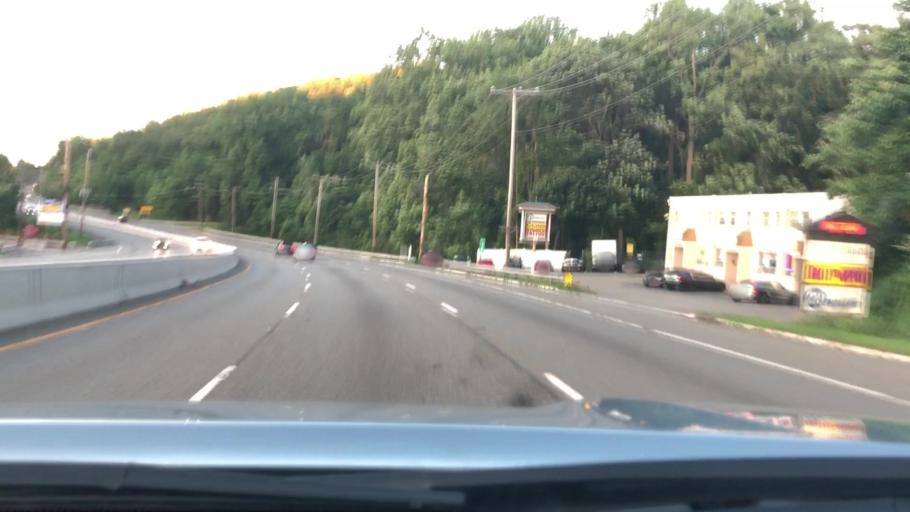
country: US
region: New Jersey
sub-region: Passaic County
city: Bloomingdale
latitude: 40.9879
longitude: -74.3234
